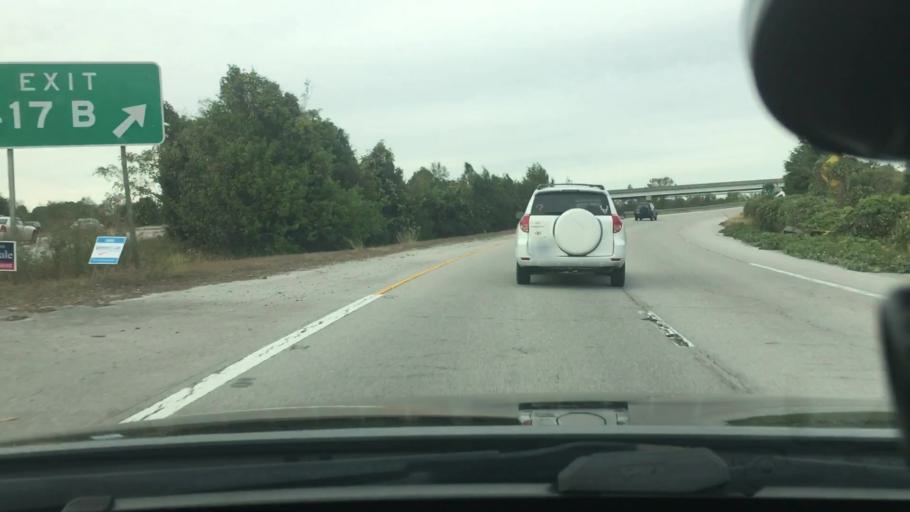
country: US
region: North Carolina
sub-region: Craven County
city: James City
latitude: 35.0899
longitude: -77.0355
